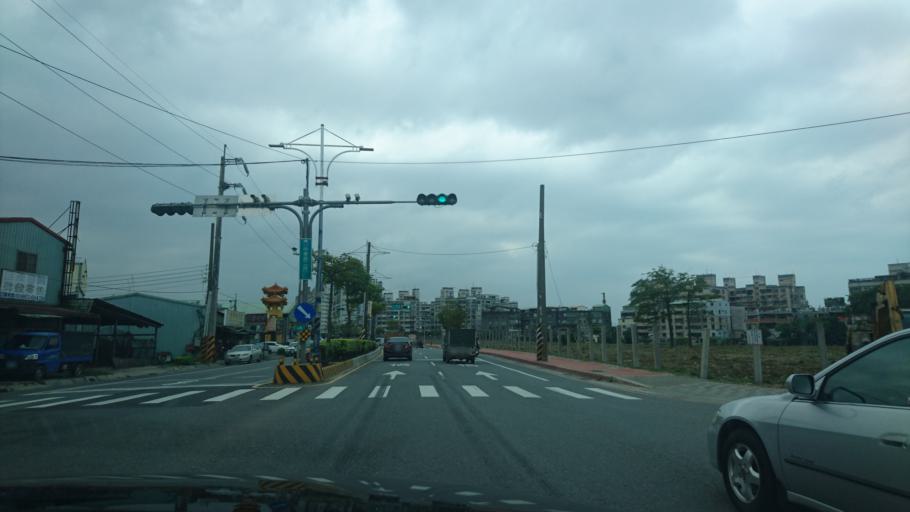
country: TW
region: Taipei
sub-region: Taipei
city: Banqiao
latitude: 25.1516
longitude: 121.4083
